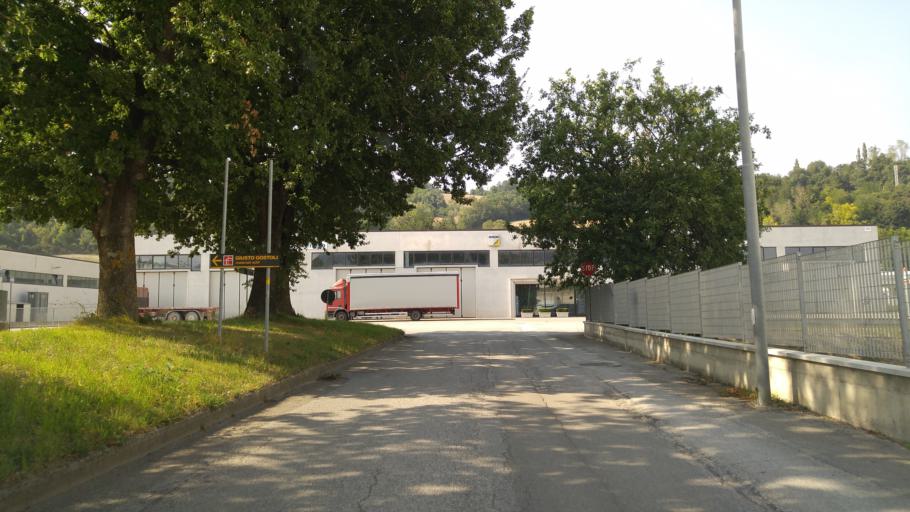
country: IT
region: The Marches
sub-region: Provincia di Pesaro e Urbino
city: Fermignano
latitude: 43.6942
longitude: 12.6511
